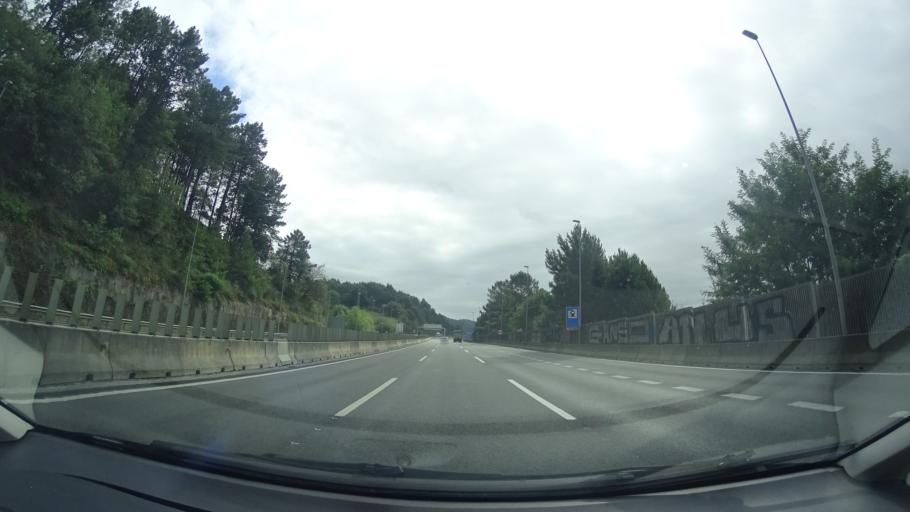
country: ES
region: Basque Country
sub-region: Bizkaia
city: Zaratamo
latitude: 43.2341
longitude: -2.8621
